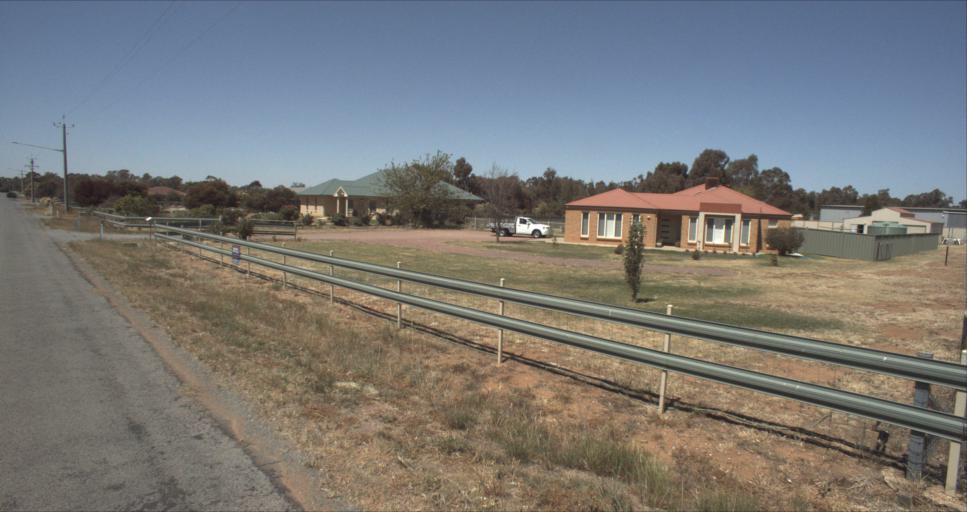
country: AU
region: New South Wales
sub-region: Leeton
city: Leeton
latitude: -34.5278
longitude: 146.3971
